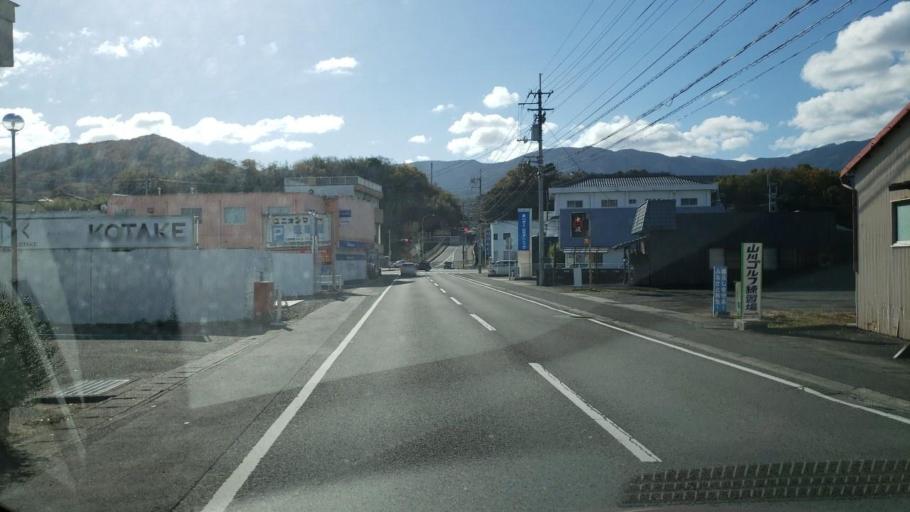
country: JP
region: Tokushima
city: Wakimachi
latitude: 34.0582
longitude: 134.2385
